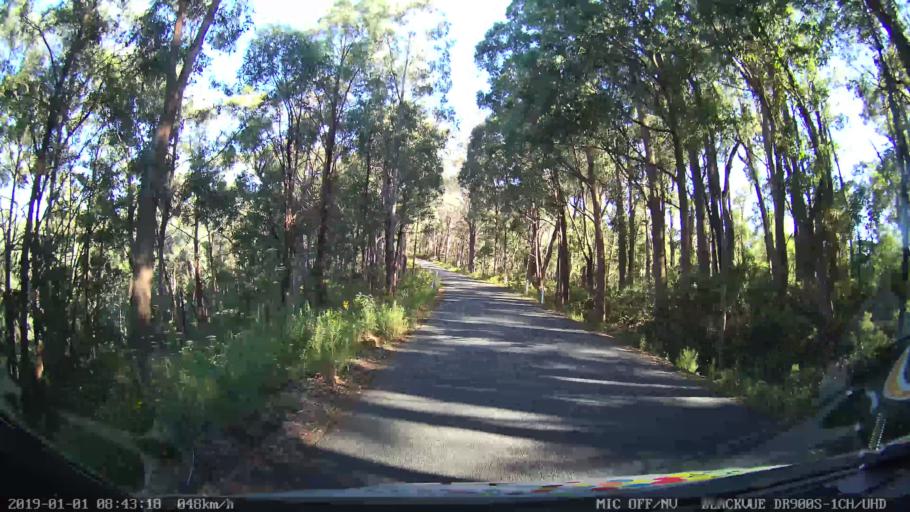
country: AU
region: New South Wales
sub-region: Snowy River
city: Jindabyne
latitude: -36.3184
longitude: 148.1934
